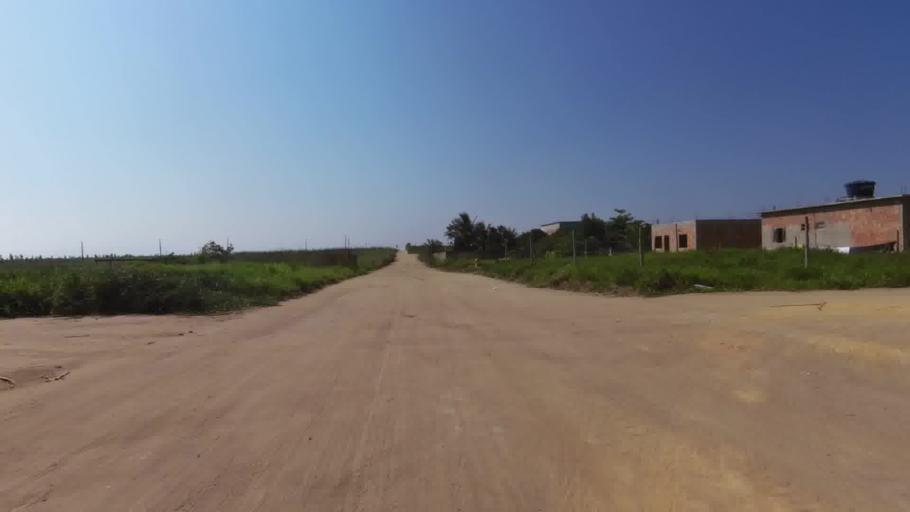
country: BR
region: Espirito Santo
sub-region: Marataizes
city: Marataizes
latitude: -21.0411
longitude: -40.8431
